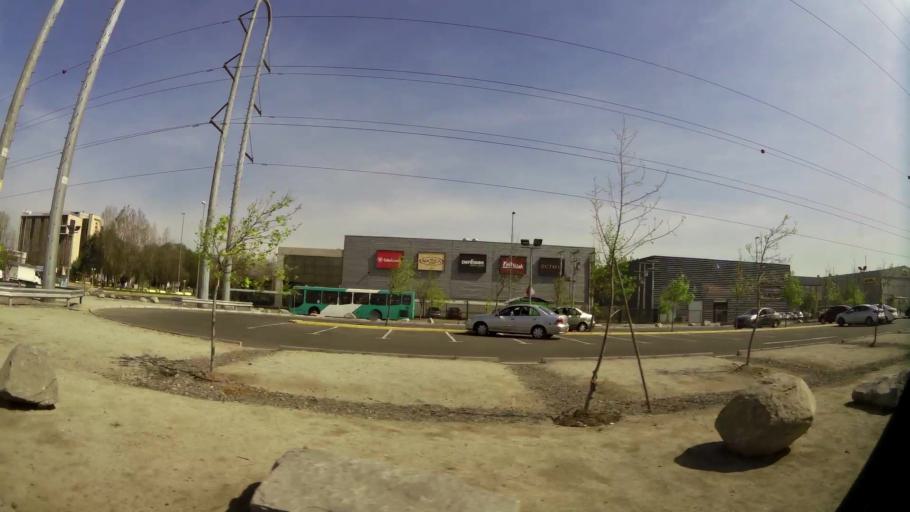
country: CL
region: Santiago Metropolitan
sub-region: Provincia de Santiago
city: Lo Prado
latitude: -33.4284
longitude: -70.7758
